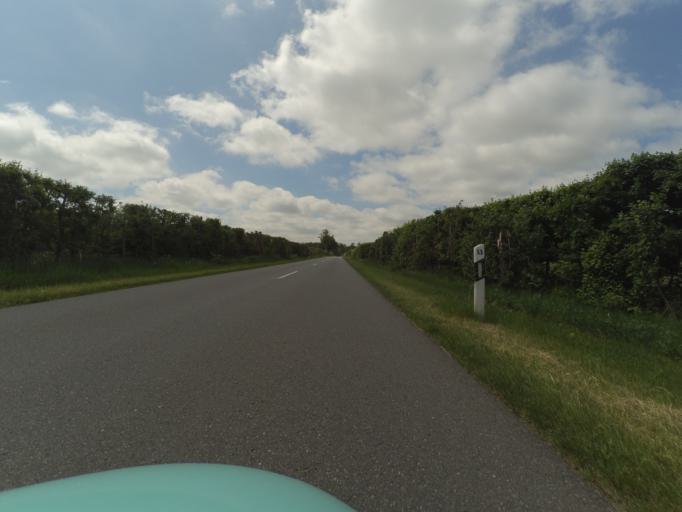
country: DE
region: Lower Saxony
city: Hillerse
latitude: 52.4269
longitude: 10.3602
